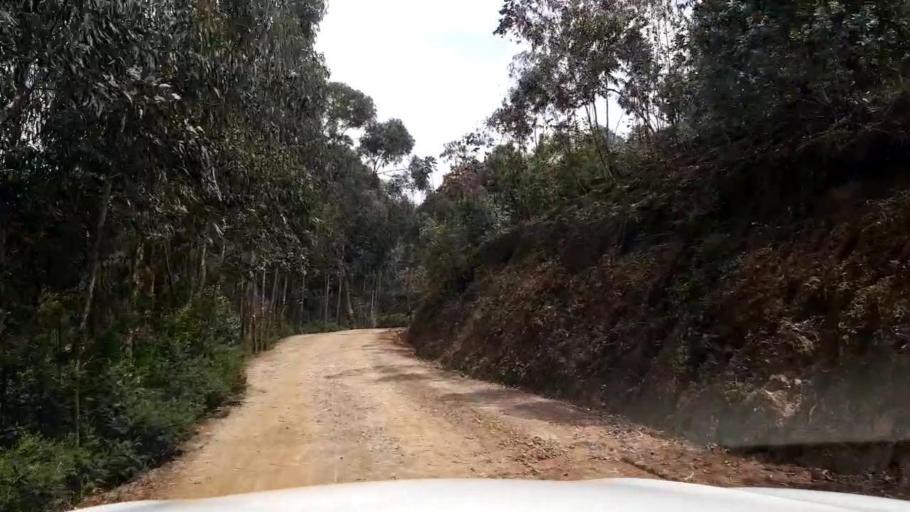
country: RW
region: Western Province
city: Kibuye
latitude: -1.9359
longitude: 29.4535
